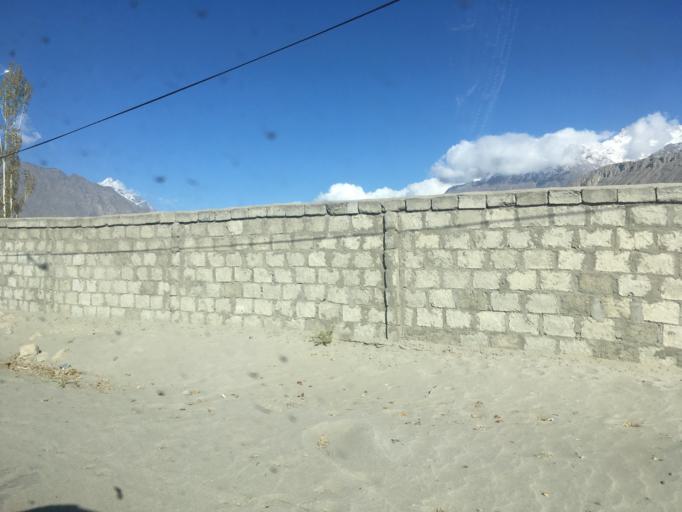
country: PK
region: Gilgit-Baltistan
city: Skardu
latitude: 35.3577
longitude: 75.5473
